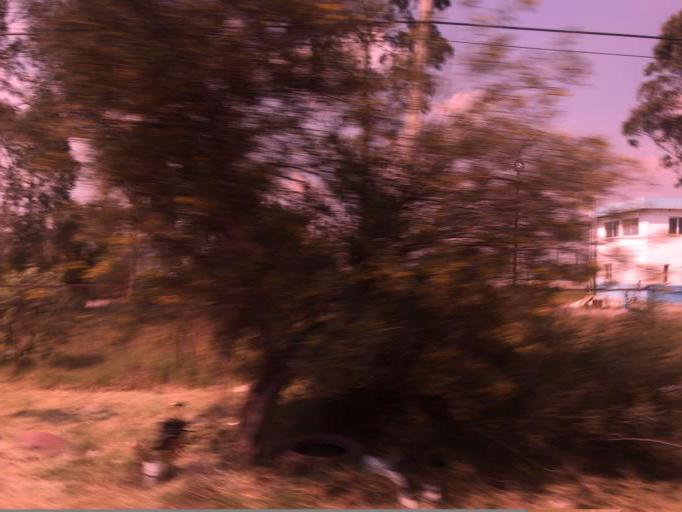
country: MX
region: Mexico
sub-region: Ciudad Nezahualcoyotl
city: Colonia Gustavo Baz Prada
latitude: 19.4698
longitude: -99.0039
